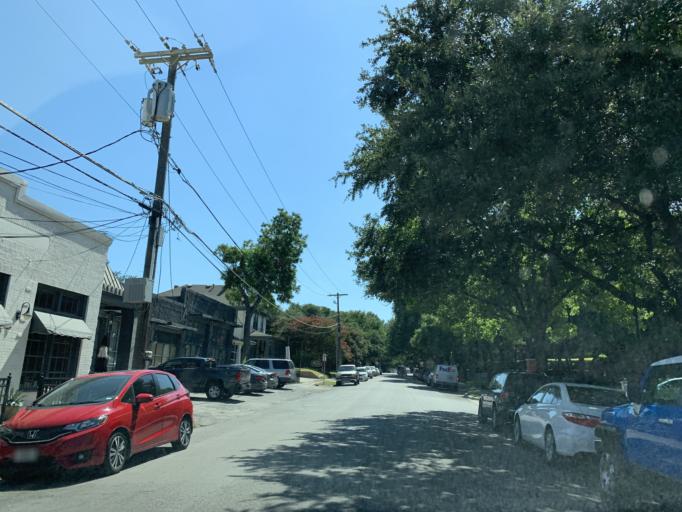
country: US
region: Texas
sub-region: Dallas County
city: Dallas
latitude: 32.7900
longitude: -96.7837
